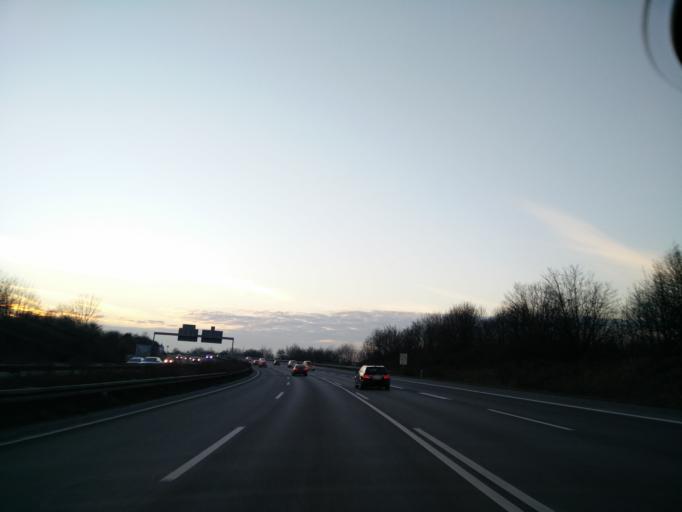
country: DE
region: North Rhine-Westphalia
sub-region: Regierungsbezirk Dusseldorf
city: Ratingen
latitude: 51.2911
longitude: 6.7935
